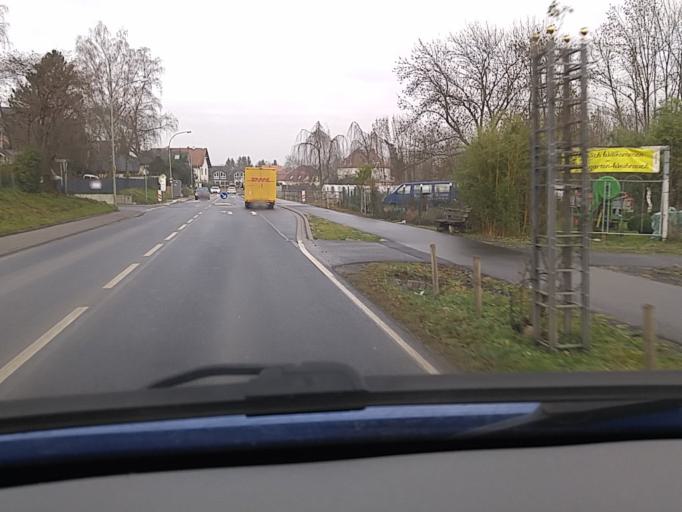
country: DE
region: Hesse
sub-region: Regierungsbezirk Darmstadt
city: Bad Nauheim
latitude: 50.3930
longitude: 8.7470
